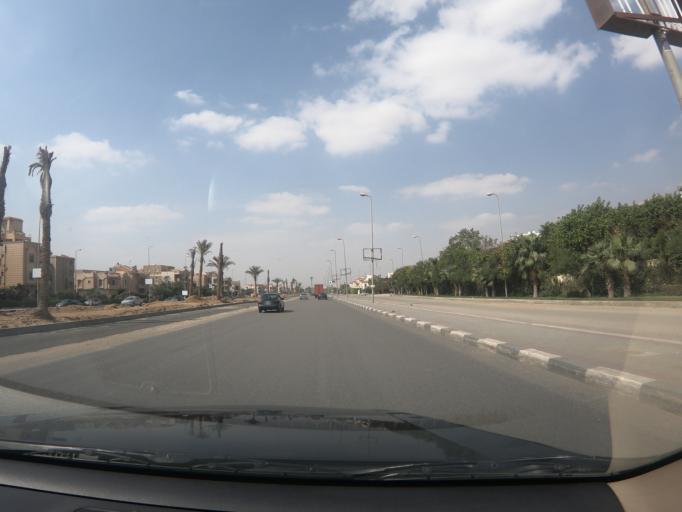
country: EG
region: Muhafazat al Qalyubiyah
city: Al Khankah
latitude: 30.0509
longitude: 31.4751
